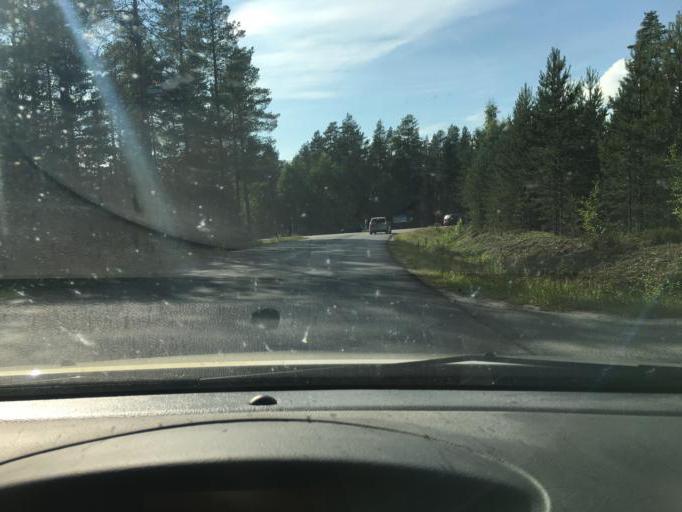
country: SE
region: Norrbotten
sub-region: Lulea Kommun
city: Gammelstad
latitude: 65.5951
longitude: 22.0501
